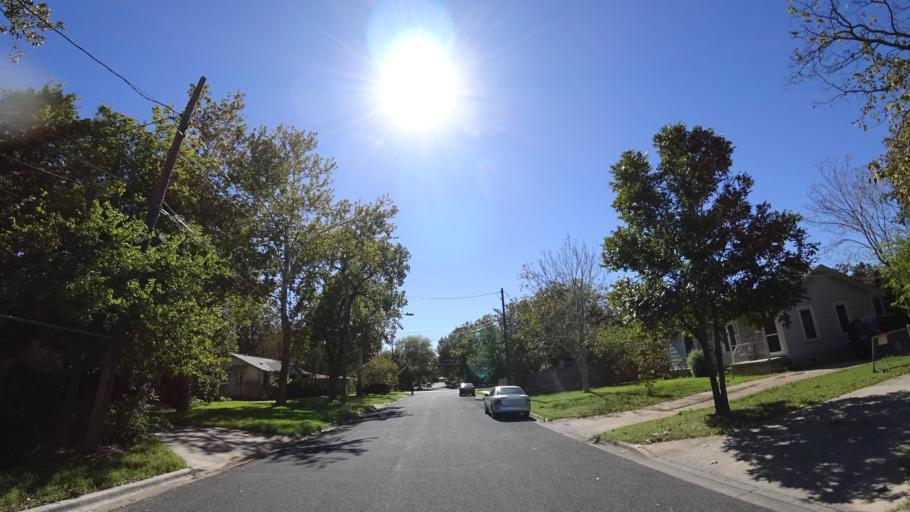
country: US
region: Texas
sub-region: Travis County
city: Rollingwood
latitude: 30.2267
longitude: -97.7859
